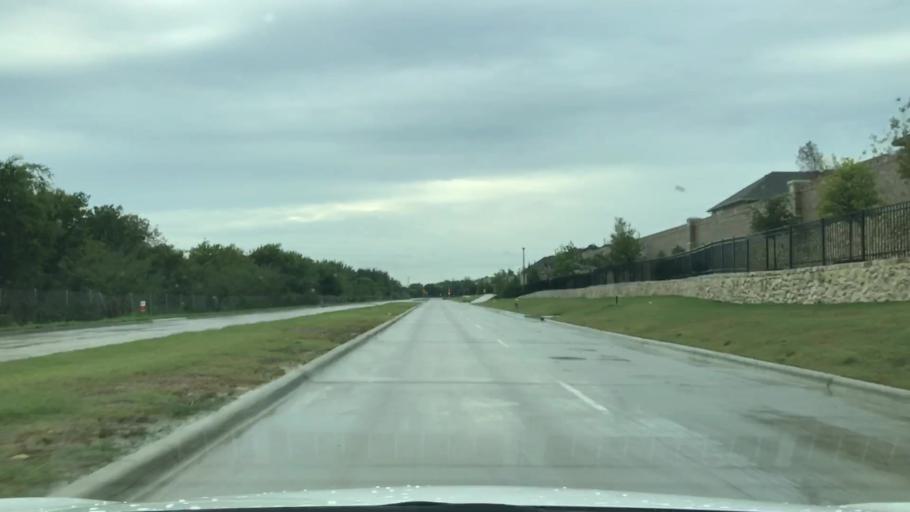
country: US
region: Texas
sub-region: Dallas County
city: Coppell
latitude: 32.9059
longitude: -97.0025
